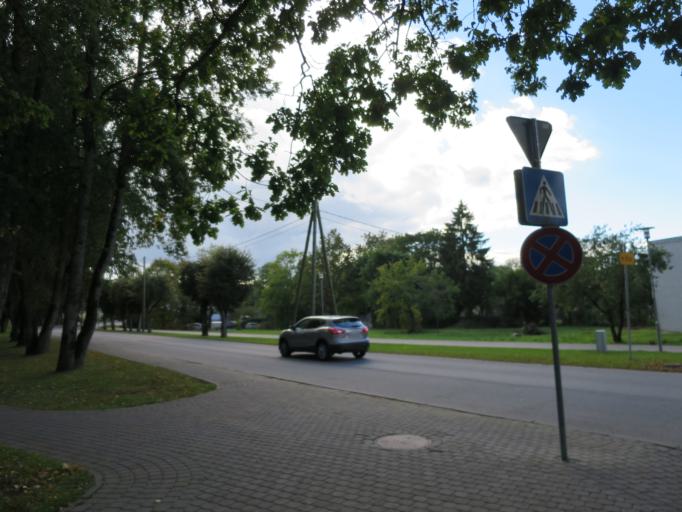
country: LV
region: Sigulda
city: Sigulda
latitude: 57.1557
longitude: 24.8504
